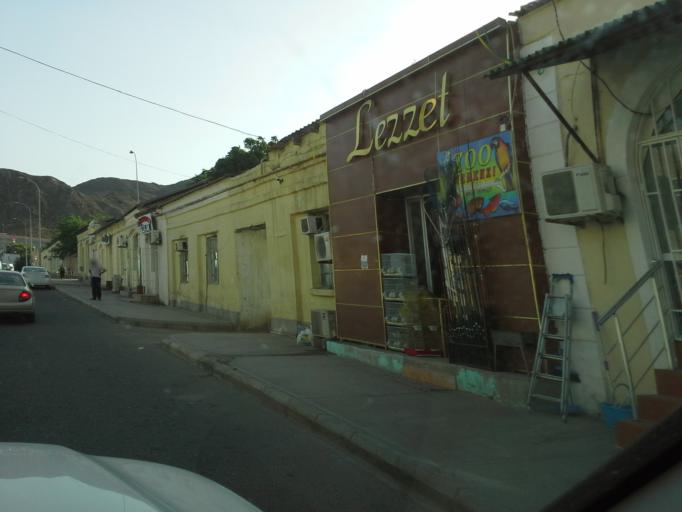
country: TM
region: Balkan
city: Turkmenbasy
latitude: 40.0022
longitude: 52.9896
